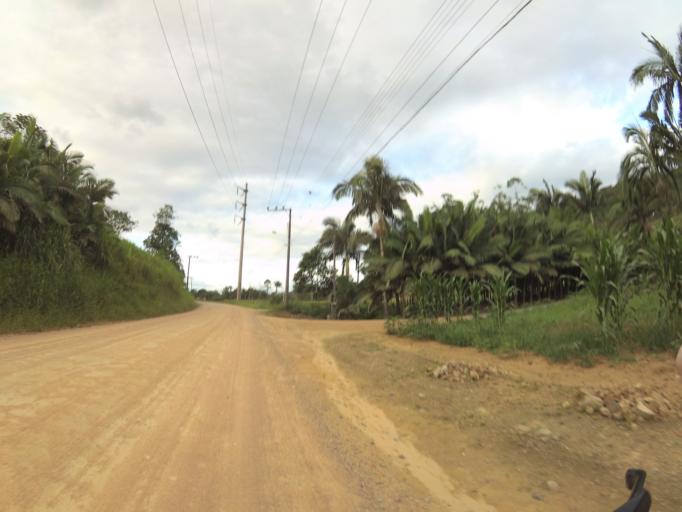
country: BR
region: Santa Catarina
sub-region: Pomerode
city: Pomerode
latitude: -26.7817
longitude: -49.1644
